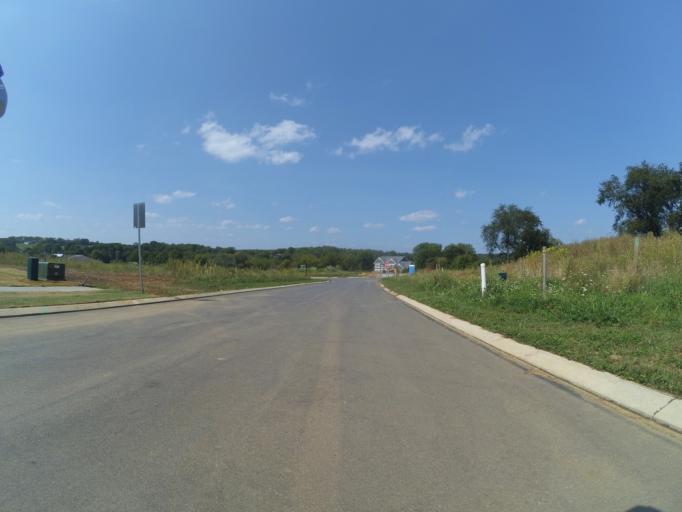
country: US
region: Pennsylvania
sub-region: Centre County
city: Houserville
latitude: 40.8322
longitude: -77.8227
